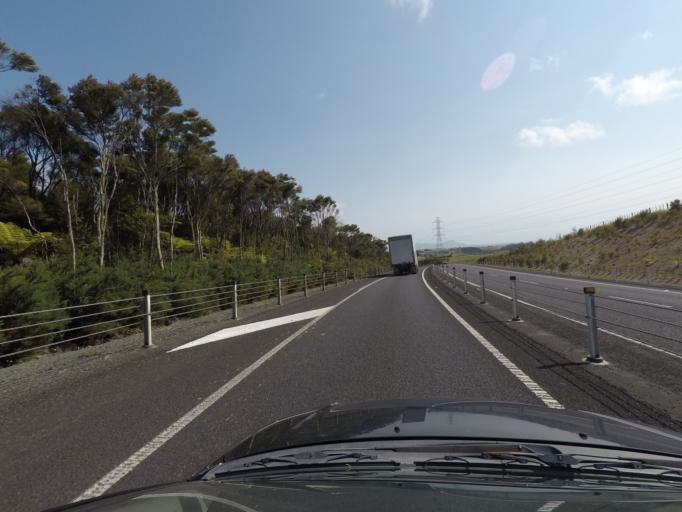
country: NZ
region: Northland
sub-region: Whangarei
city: Ruakaka
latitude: -36.0478
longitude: 174.4164
